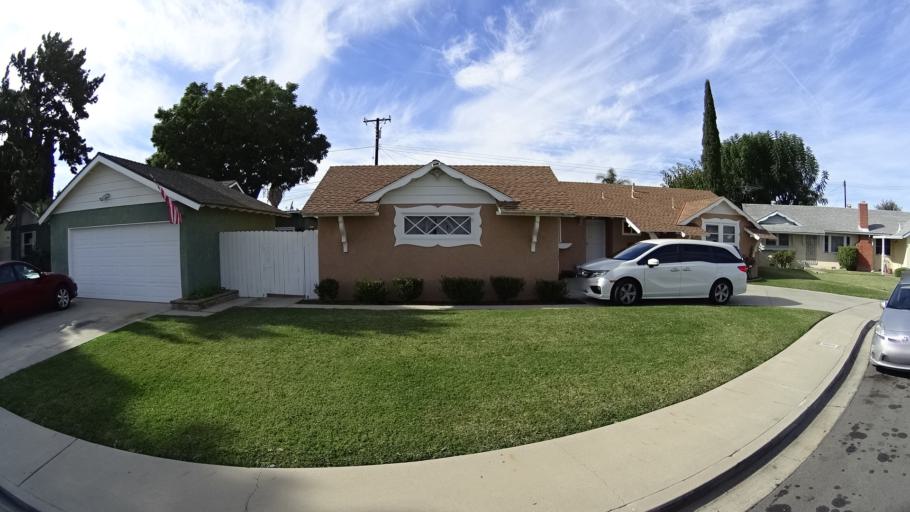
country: US
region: California
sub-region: Orange County
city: Garden Grove
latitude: 33.7630
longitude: -117.9099
